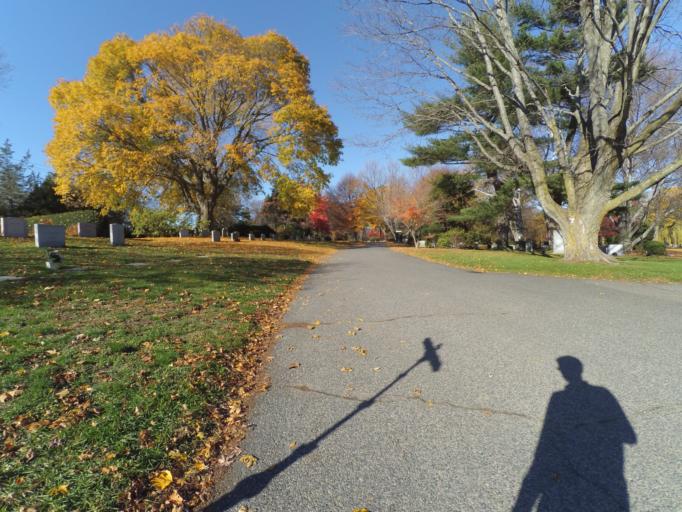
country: US
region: Massachusetts
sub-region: Middlesex County
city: Watertown
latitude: 42.3672
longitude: -71.1479
